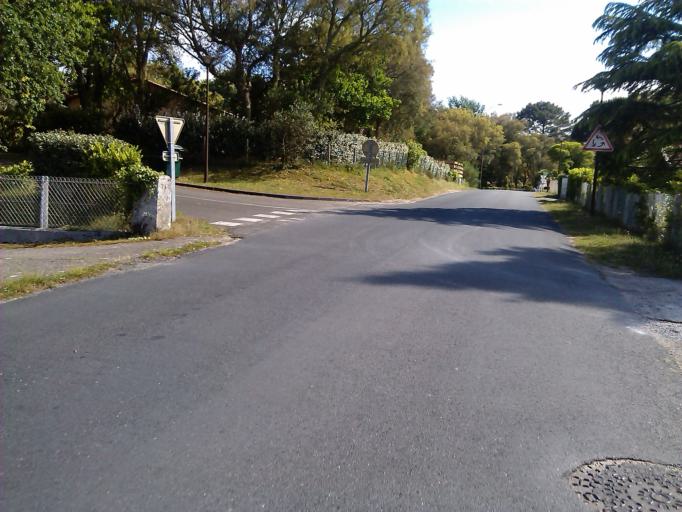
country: FR
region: Aquitaine
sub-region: Departement des Landes
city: Leon
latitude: 43.8526
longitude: -1.3591
